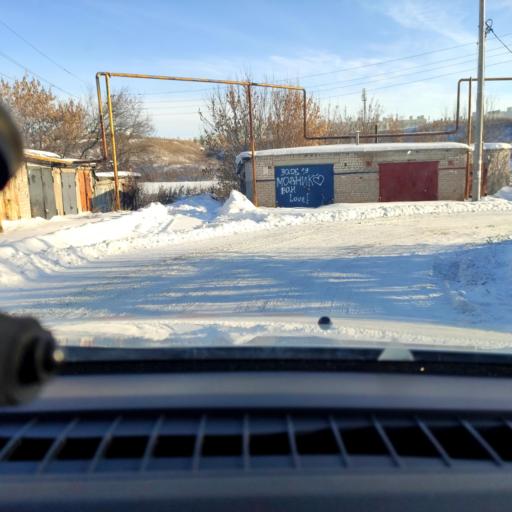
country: RU
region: Samara
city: Petra-Dubrava
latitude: 53.3106
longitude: 50.3022
